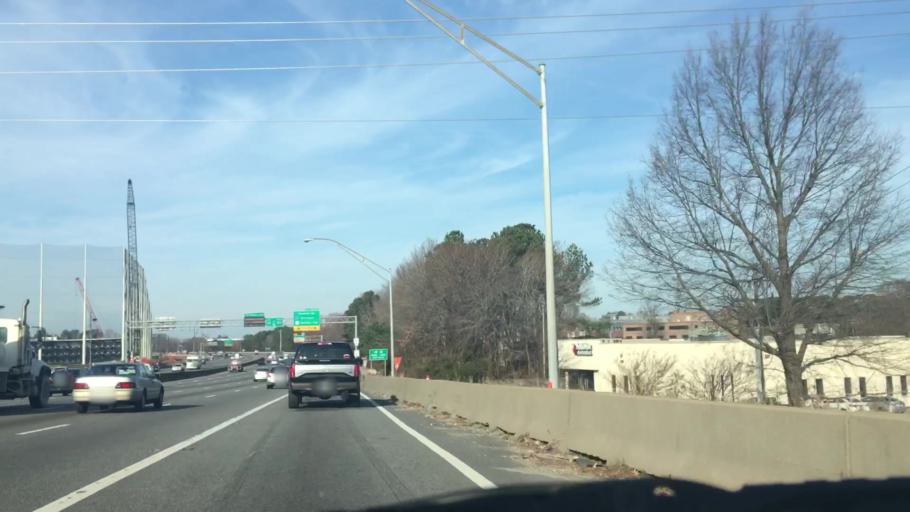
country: US
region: Virginia
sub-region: City of Chesapeake
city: Chesapeake
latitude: 36.8415
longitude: -76.1638
